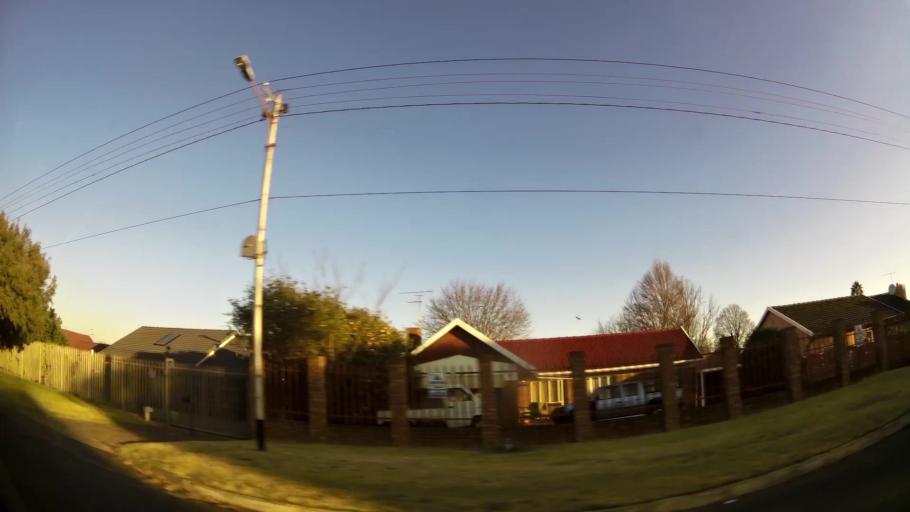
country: ZA
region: Gauteng
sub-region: City of Johannesburg Metropolitan Municipality
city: Roodepoort
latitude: -26.1523
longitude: 27.8861
